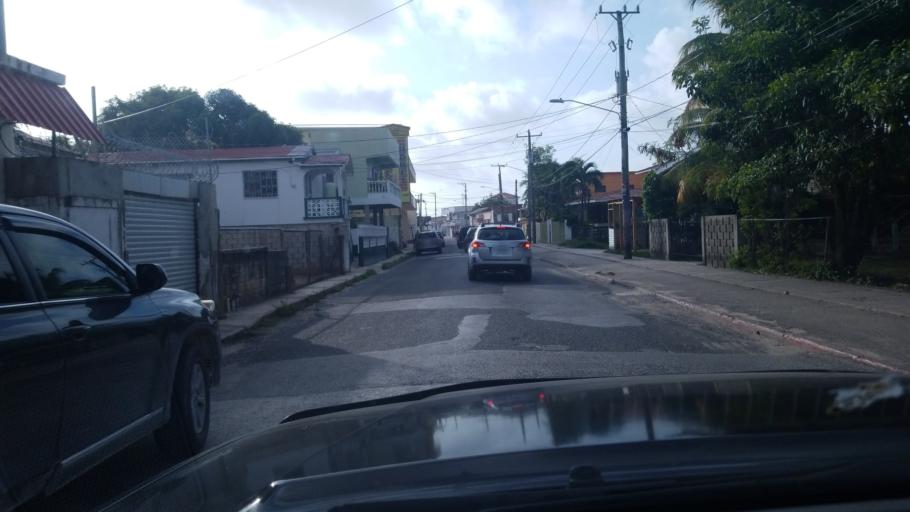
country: BZ
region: Belize
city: Belize City
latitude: 17.4950
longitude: -88.1964
